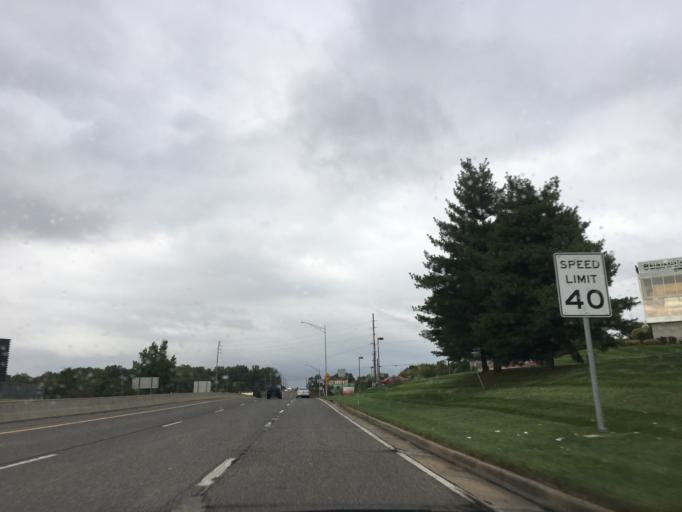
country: US
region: Missouri
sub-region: Saint Louis County
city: Maryland Heights
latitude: 38.7088
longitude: -90.4086
